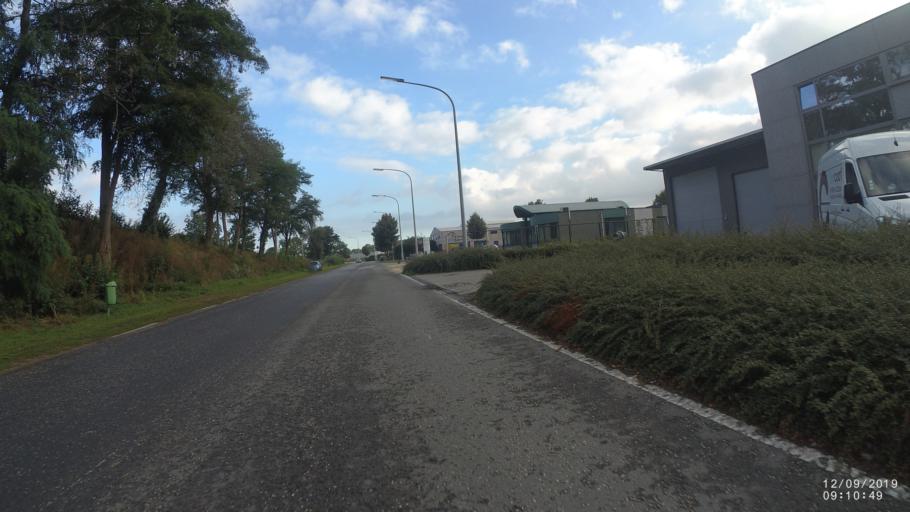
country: BE
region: Flanders
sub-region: Provincie Oost-Vlaanderen
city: Lovendegem
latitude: 51.0930
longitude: 3.6378
